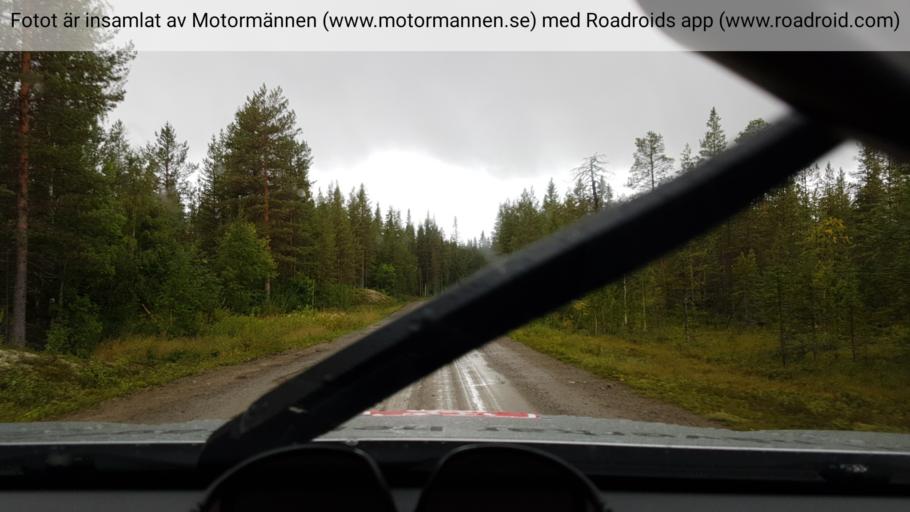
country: SE
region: Vaesterbotten
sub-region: Storumans Kommun
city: Storuman
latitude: 64.9448
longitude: 17.5132
